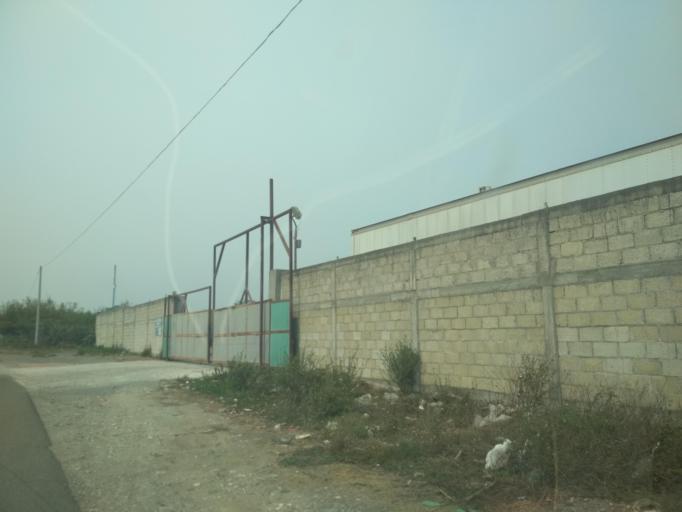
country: MX
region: Veracruz
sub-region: Veracruz
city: Delfino Victoria (Santa Fe)
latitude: 19.1927
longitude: -96.2751
